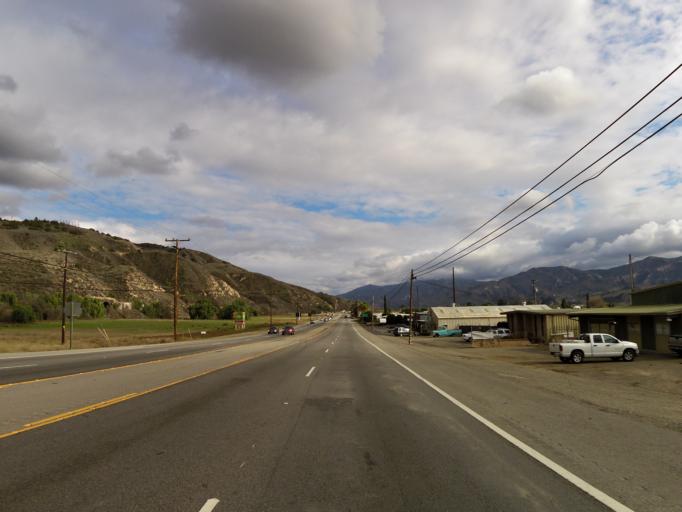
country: US
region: California
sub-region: Ventura County
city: Fillmore
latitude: 34.3991
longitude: -118.9020
